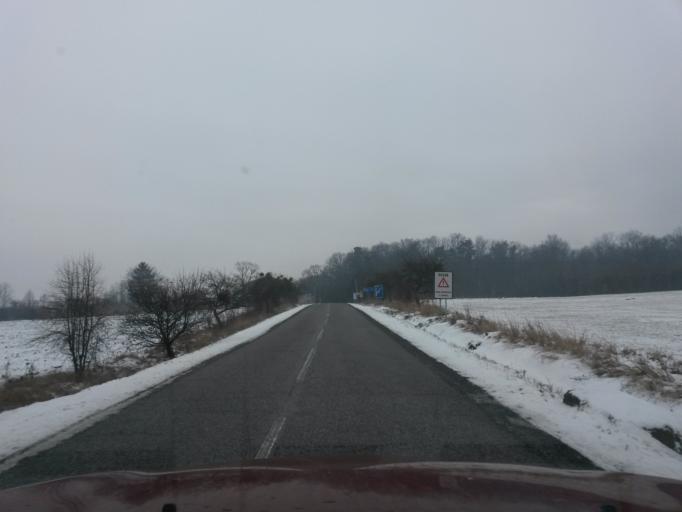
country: SK
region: Kosicky
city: Secovce
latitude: 48.7972
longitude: 21.4822
